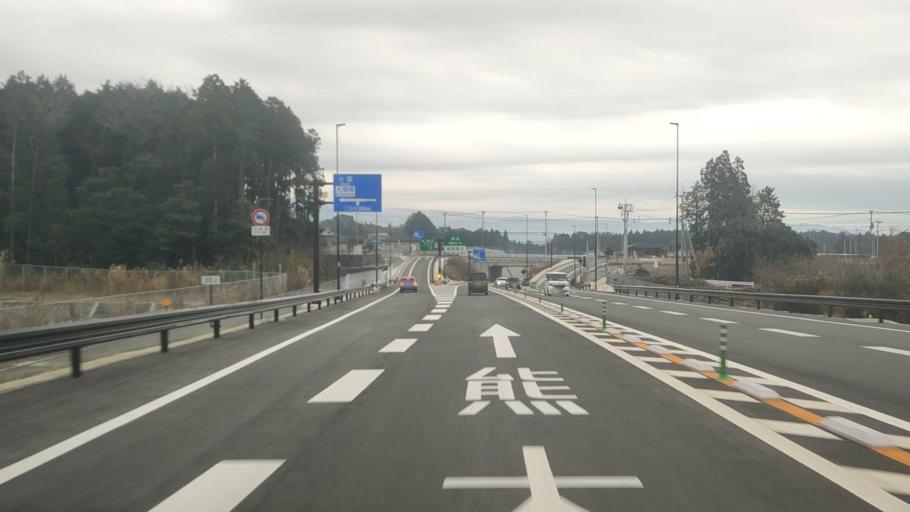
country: JP
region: Kumamoto
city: Ozu
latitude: 32.8924
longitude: 130.8962
